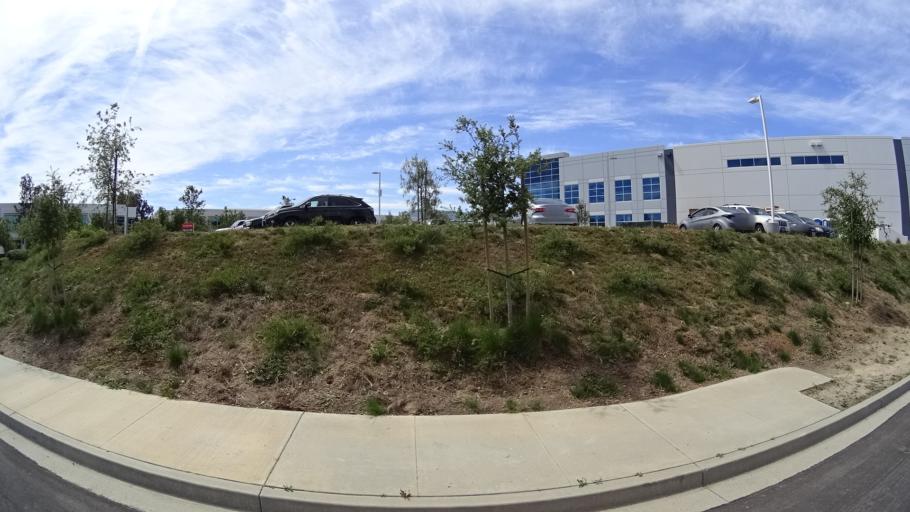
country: US
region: California
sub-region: Ventura County
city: Casa Conejo
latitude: 34.2044
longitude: -118.9286
